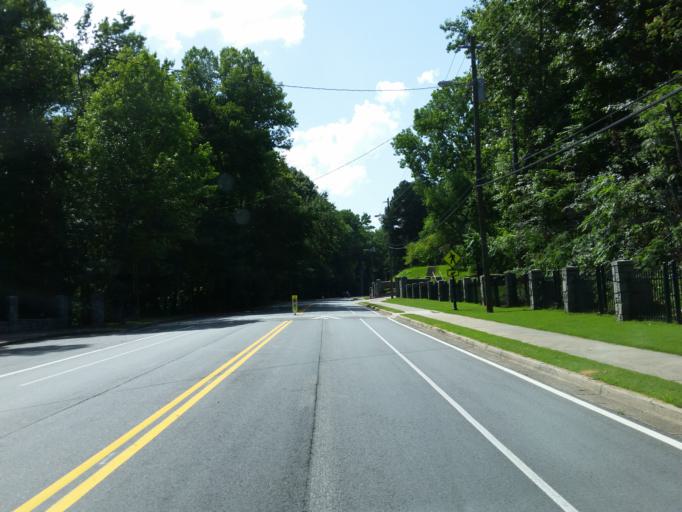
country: US
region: Georgia
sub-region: Cobb County
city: Fair Oaks
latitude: 33.9304
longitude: -84.5135
